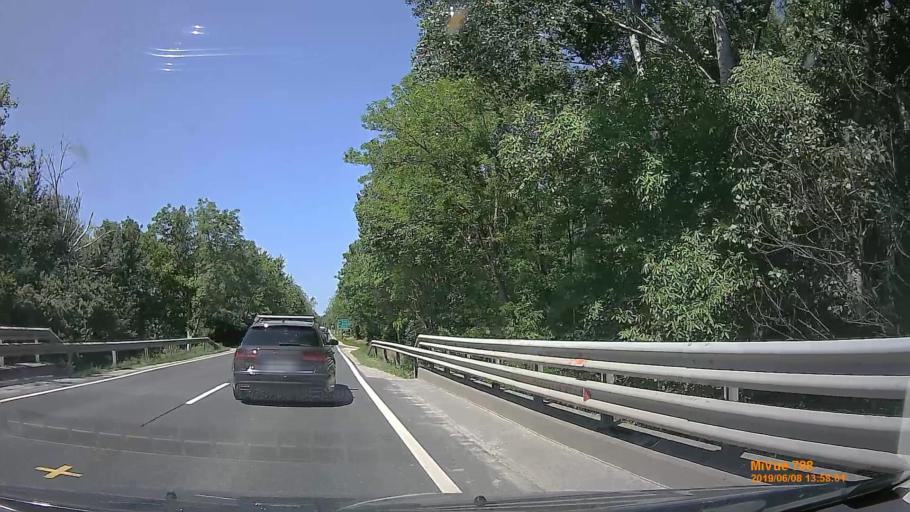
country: HU
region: Vas
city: Sarvar
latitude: 47.3733
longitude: 16.8850
